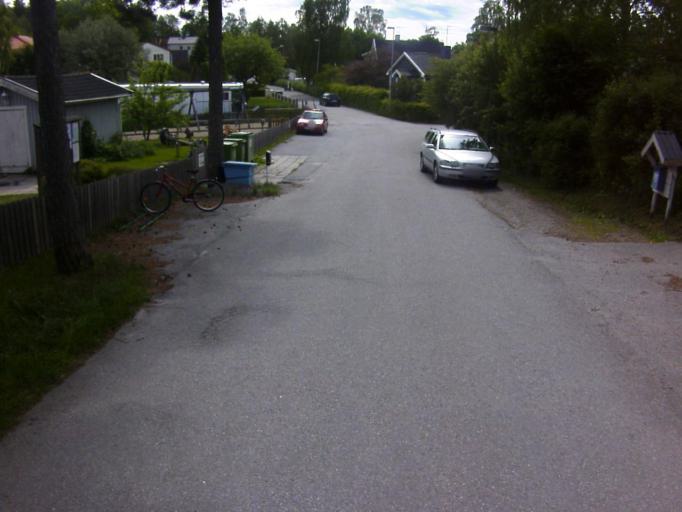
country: SE
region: Soedermanland
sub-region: Eskilstuna Kommun
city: Skogstorp
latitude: 59.3256
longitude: 16.4869
